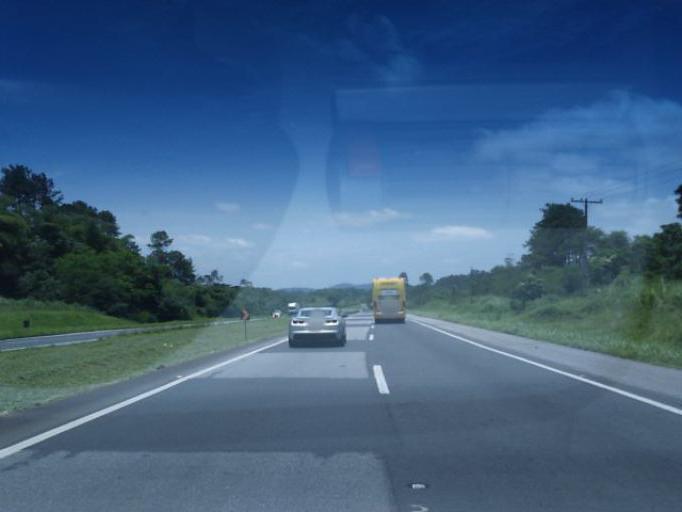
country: BR
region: Sao Paulo
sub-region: Miracatu
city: Miracatu
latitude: -24.2798
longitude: -47.4247
